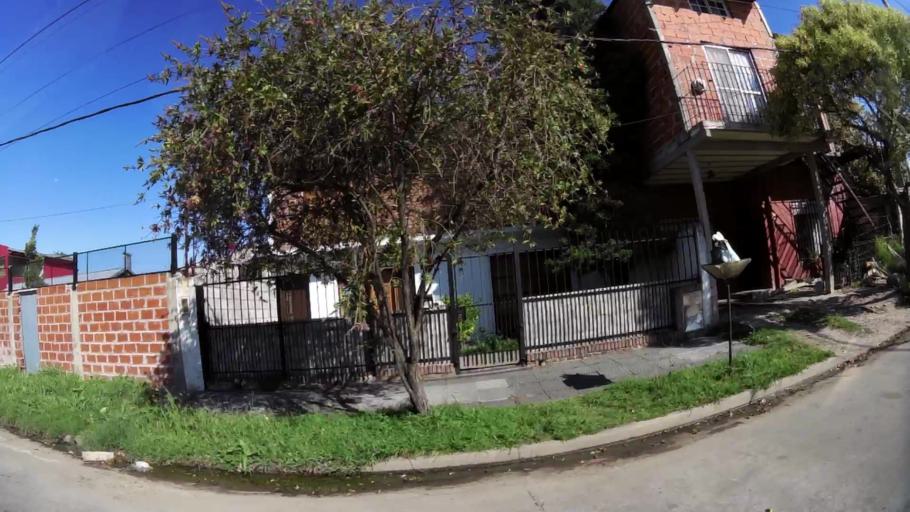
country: AR
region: Buenos Aires
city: Hurlingham
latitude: -34.5512
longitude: -58.6082
